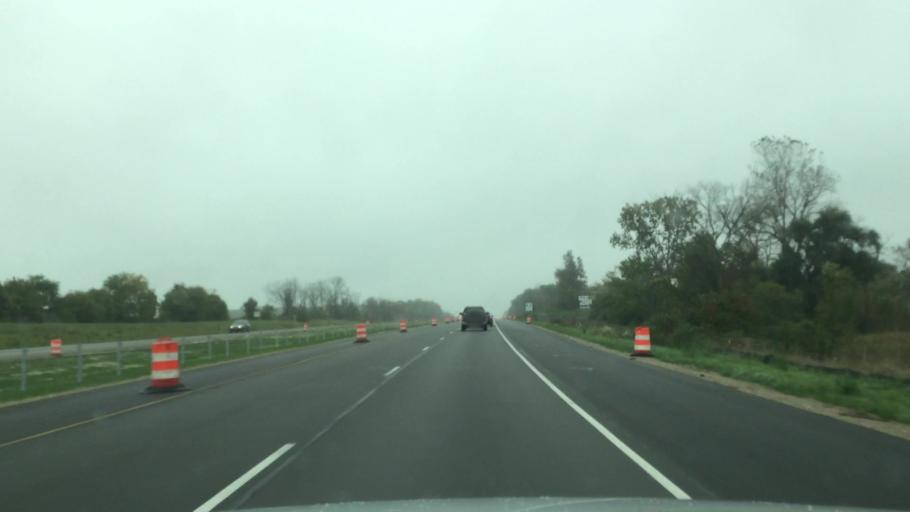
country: US
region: Michigan
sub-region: Van Buren County
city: Decatur
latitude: 42.1955
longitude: -86.0293
